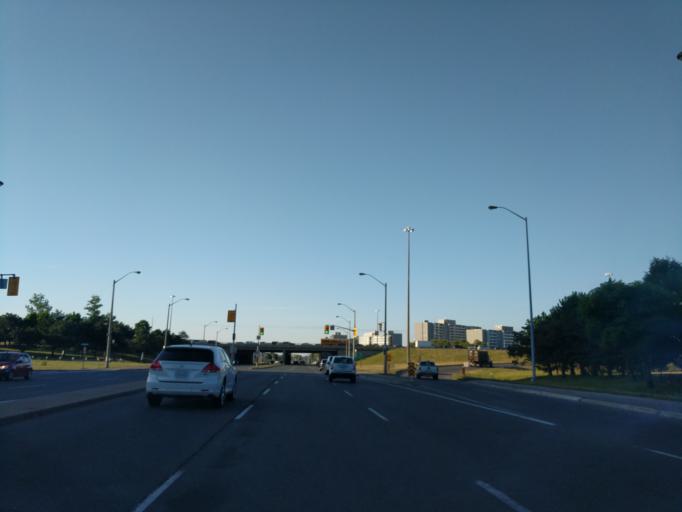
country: CA
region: Ontario
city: Scarborough
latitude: 43.7768
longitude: -79.2854
